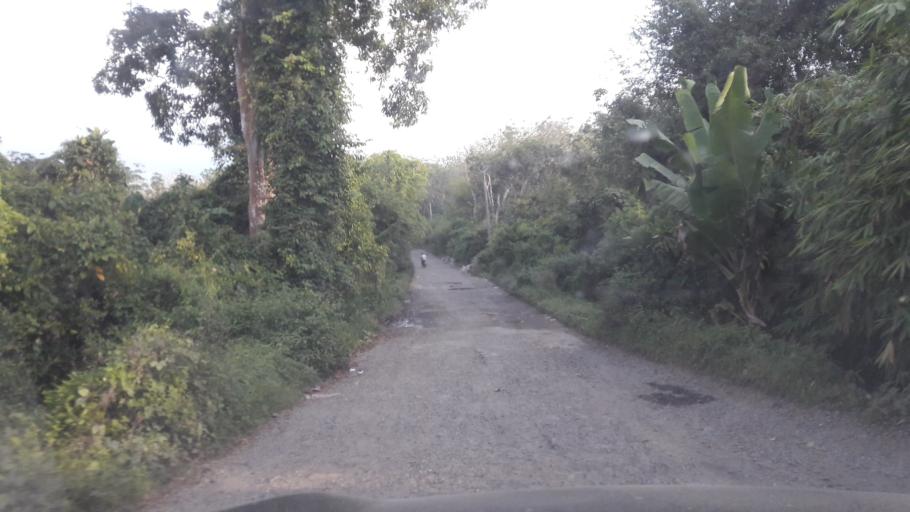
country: ID
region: South Sumatra
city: Gunungmenang
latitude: -3.3128
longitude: 104.0925
